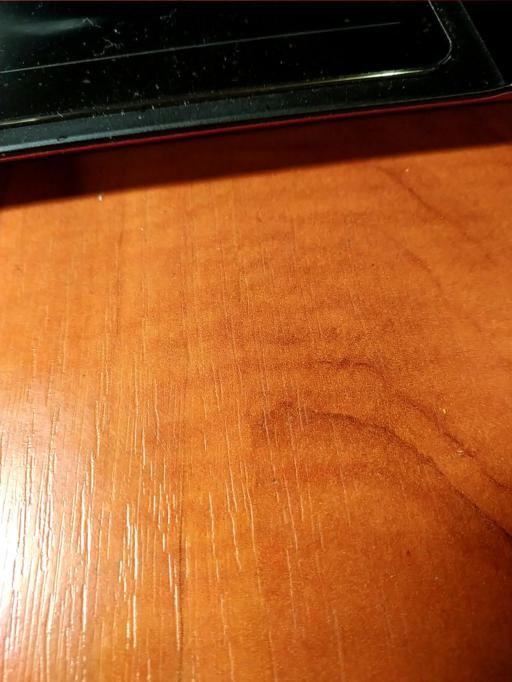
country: RU
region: Smolensk
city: Yartsevo
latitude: 55.4351
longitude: 32.7802
